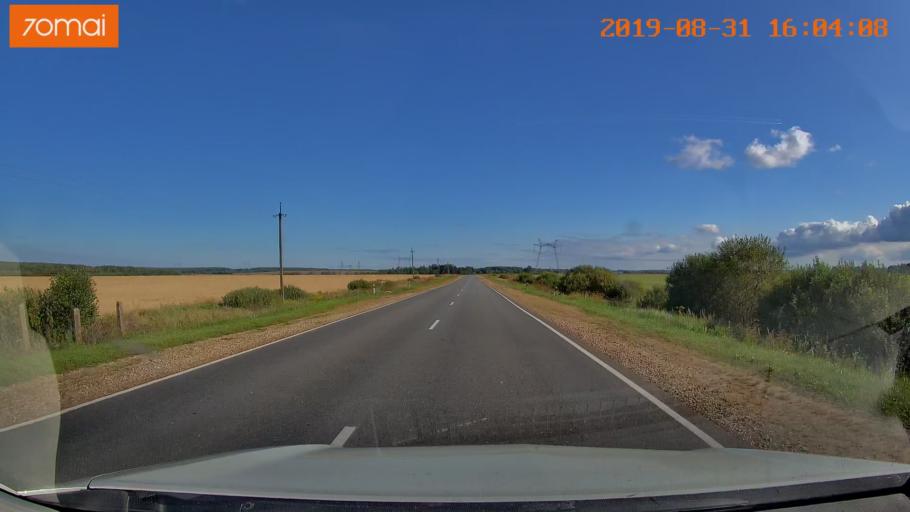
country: RU
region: Kaluga
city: Yukhnov
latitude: 54.6579
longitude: 35.3239
